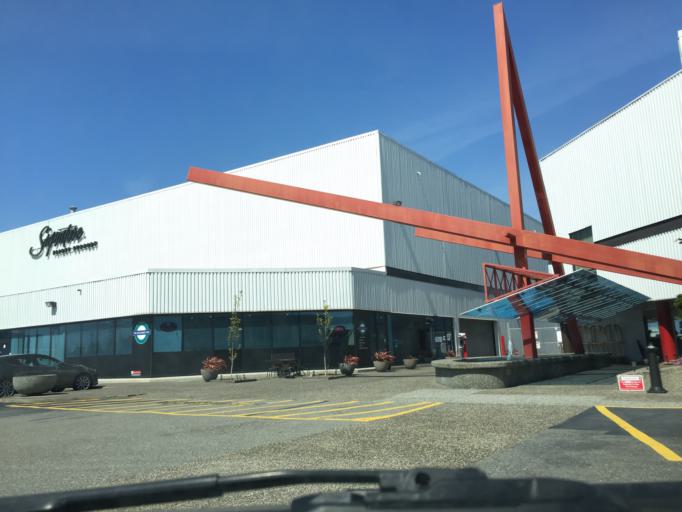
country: CA
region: British Columbia
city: Richmond
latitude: 49.1809
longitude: -123.1647
